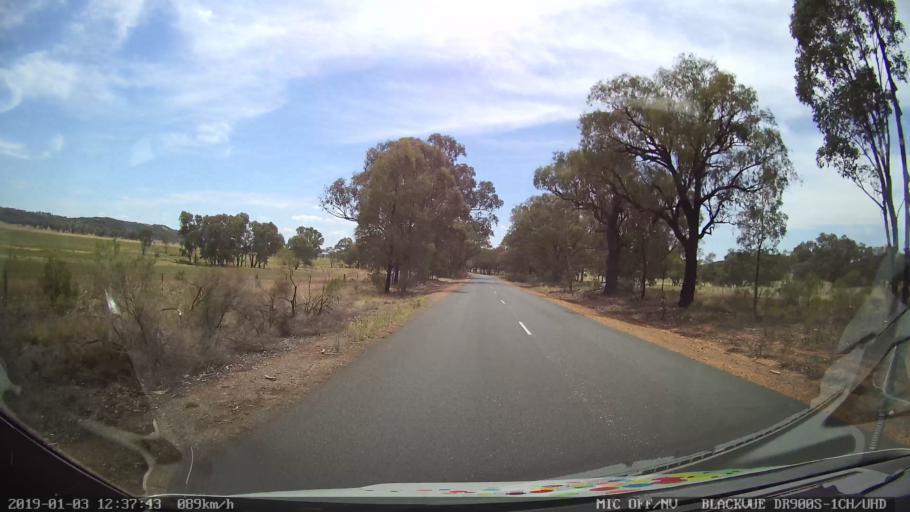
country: AU
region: New South Wales
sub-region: Weddin
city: Grenfell
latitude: -33.8401
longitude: 148.1873
